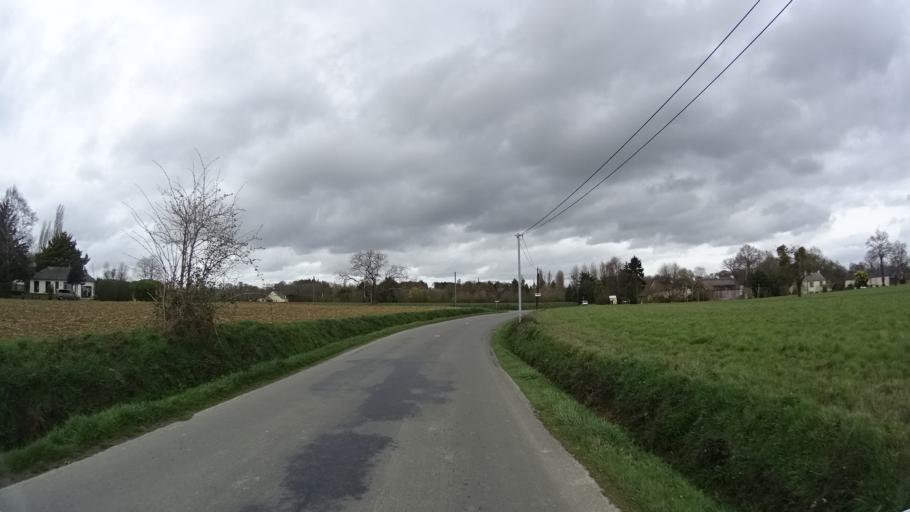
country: FR
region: Brittany
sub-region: Departement d'Ille-et-Vilaine
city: Saint-Gilles
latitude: 48.1676
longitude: -1.8301
